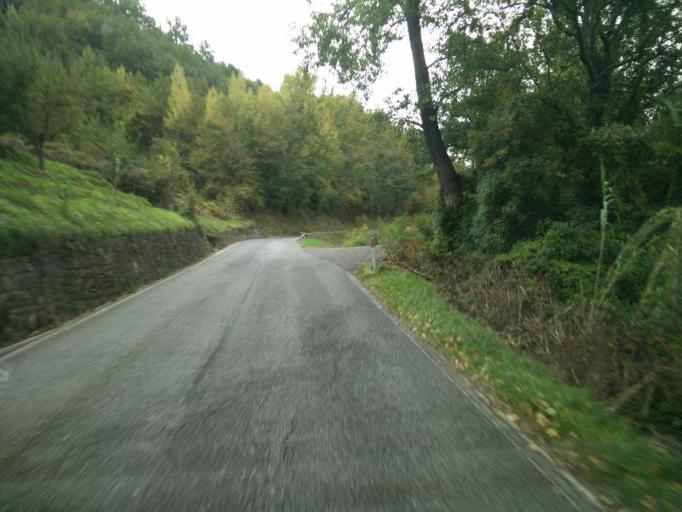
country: IT
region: Tuscany
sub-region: Provincia di Massa-Carrara
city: Casola in Lunigiana
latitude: 44.1892
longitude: 10.1396
